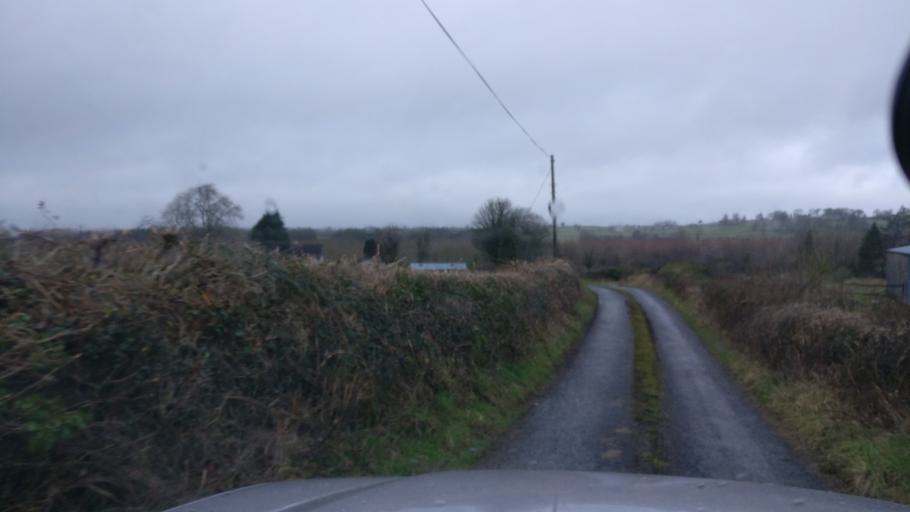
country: IE
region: Connaught
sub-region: County Galway
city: Loughrea
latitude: 53.1740
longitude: -8.6122
